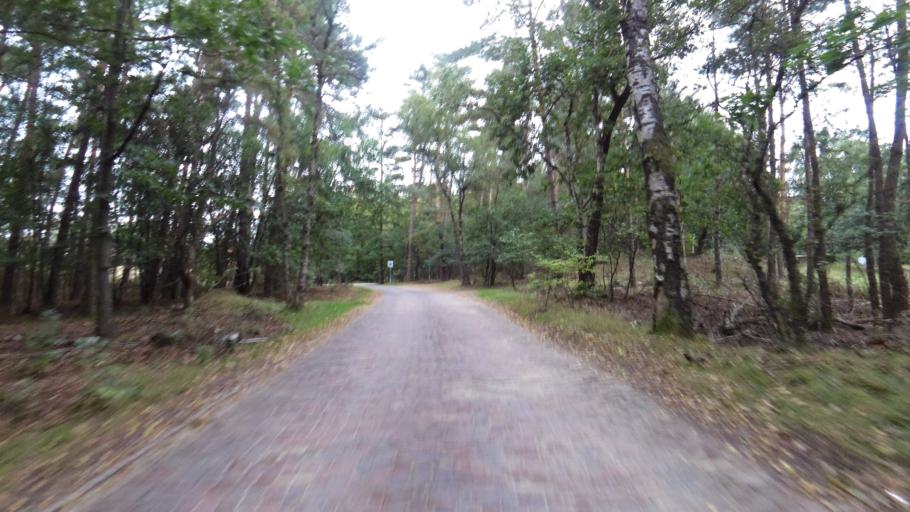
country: NL
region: Gelderland
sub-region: Gemeente Ede
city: Harskamp
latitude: 52.1738
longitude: 5.8271
